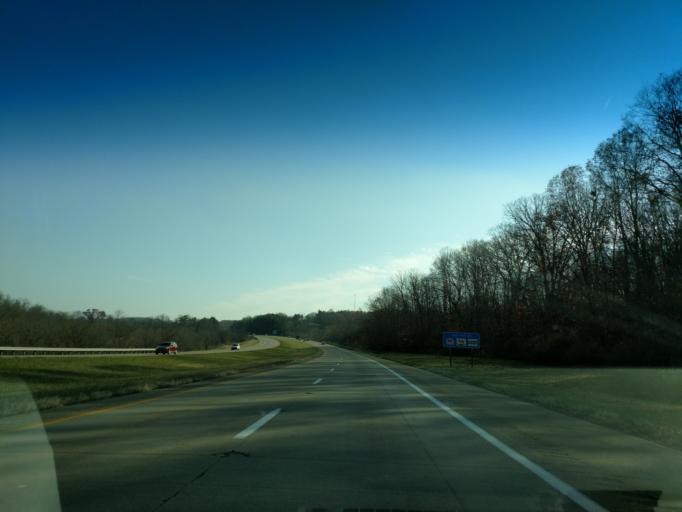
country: US
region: Ohio
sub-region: Noble County
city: Caldwell
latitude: 39.7627
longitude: -81.5429
